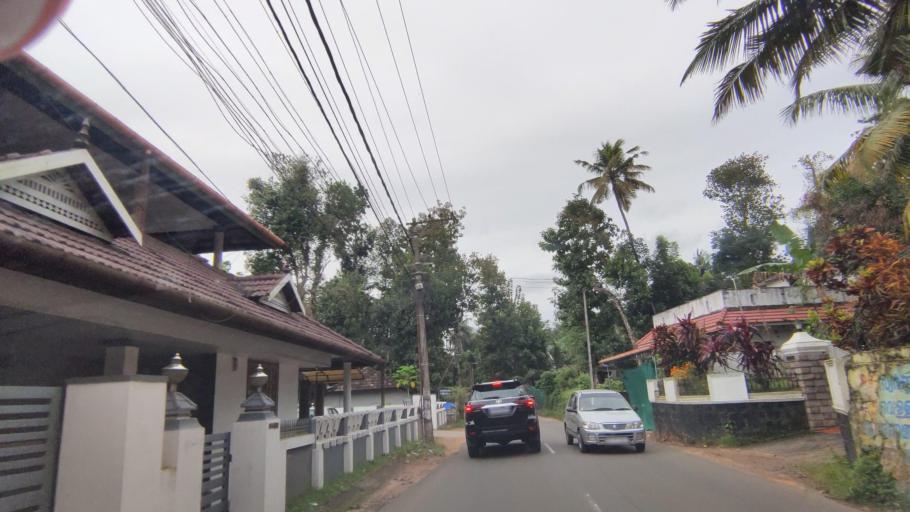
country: IN
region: Kerala
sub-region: Kottayam
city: Kottayam
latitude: 9.6826
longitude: 76.5056
